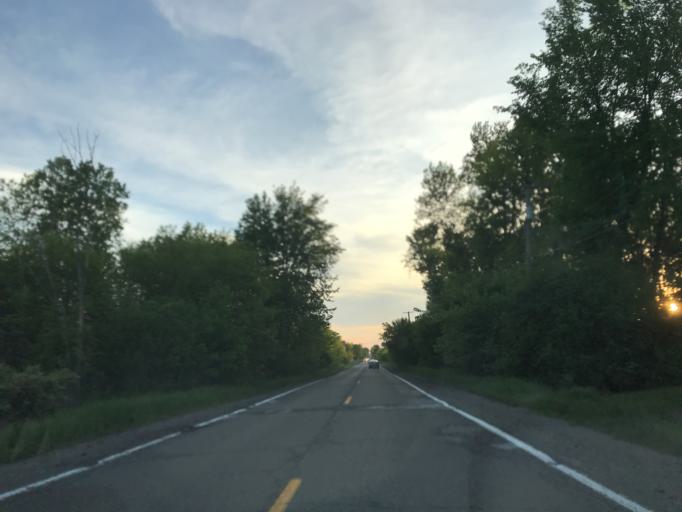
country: US
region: Michigan
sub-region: Wayne County
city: Northville
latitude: 42.4350
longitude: -83.5592
